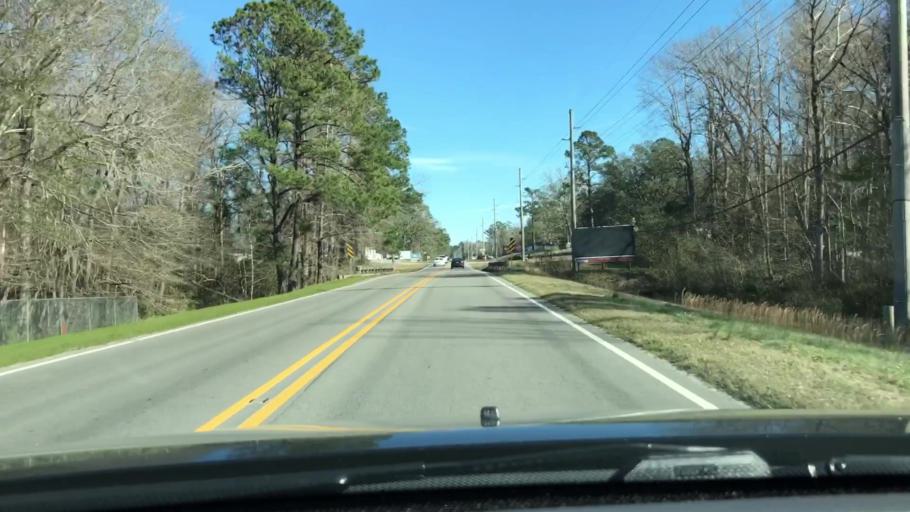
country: US
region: North Carolina
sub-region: Brunswick County
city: Shallotte
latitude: 33.9607
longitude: -78.4092
